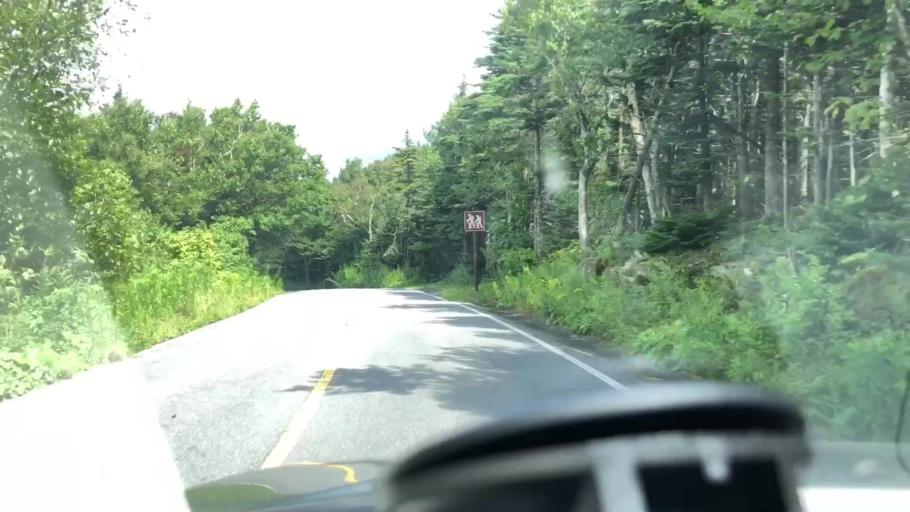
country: US
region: Massachusetts
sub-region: Berkshire County
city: Adams
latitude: 42.6425
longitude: -73.1636
